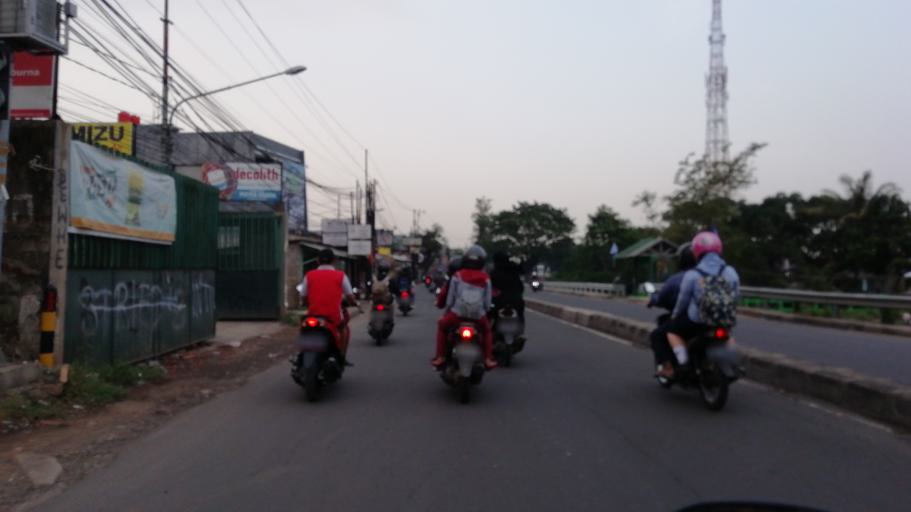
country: ID
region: West Java
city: Cibinong
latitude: -6.4498
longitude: 106.8533
